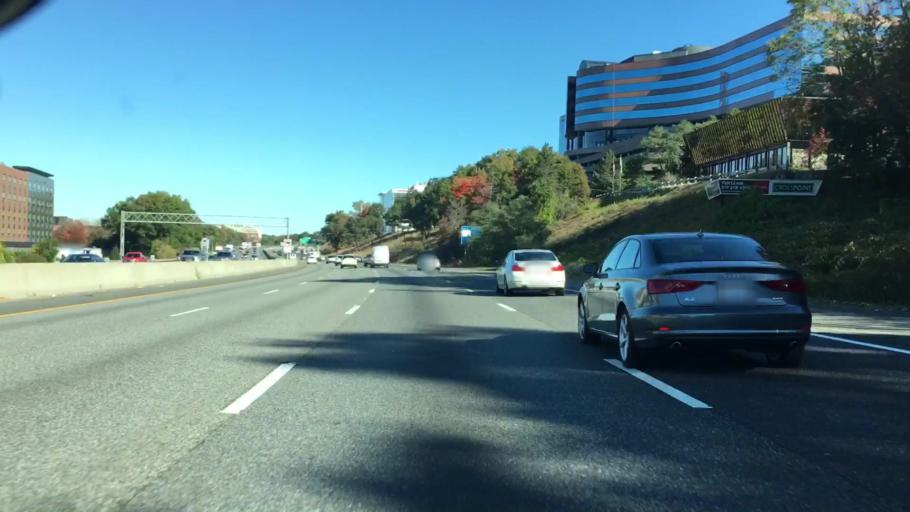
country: US
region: Massachusetts
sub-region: Middlesex County
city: Waltham
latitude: 42.3874
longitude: -71.2618
